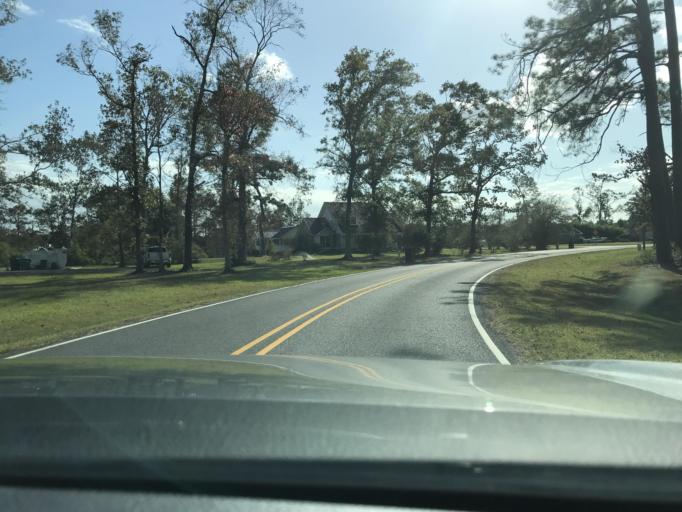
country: US
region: Louisiana
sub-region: Calcasieu Parish
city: Westlake
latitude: 30.3197
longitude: -93.2901
